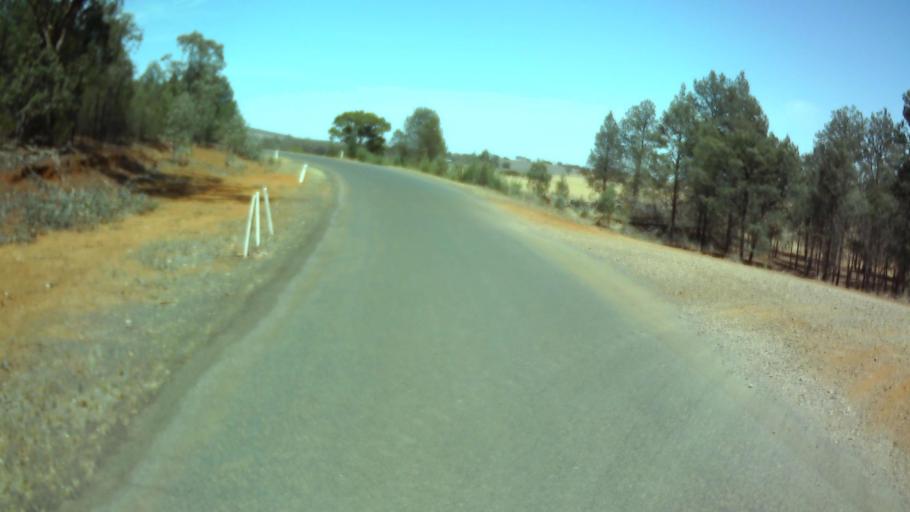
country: AU
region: New South Wales
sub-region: Weddin
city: Grenfell
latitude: -33.8615
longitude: 148.0150
